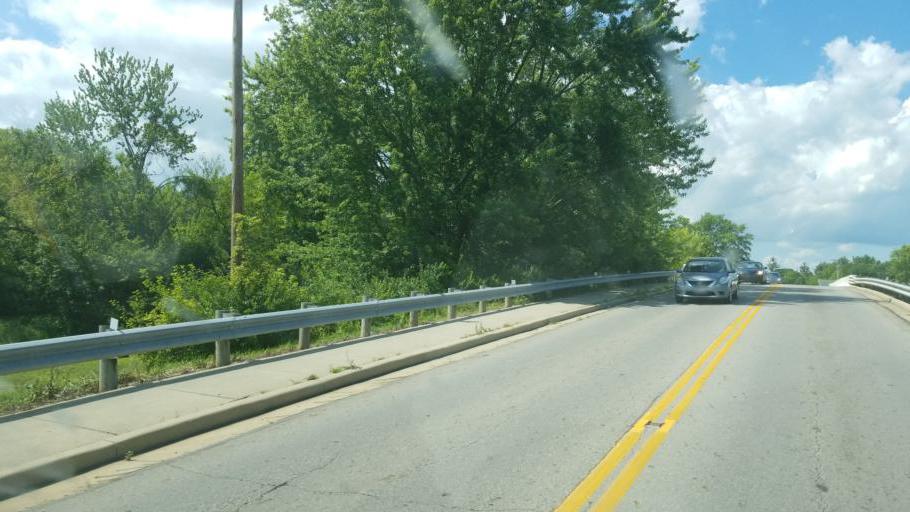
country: US
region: Ohio
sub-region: Highland County
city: Greenfield
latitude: 39.3458
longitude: -83.3900
